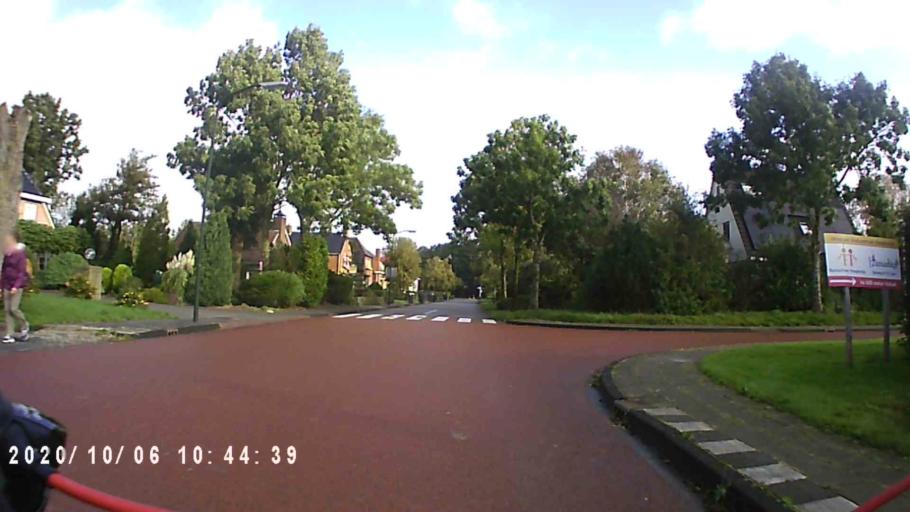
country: NL
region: Groningen
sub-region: Gemeente Zuidhorn
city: Oldehove
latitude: 53.3567
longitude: 6.4262
